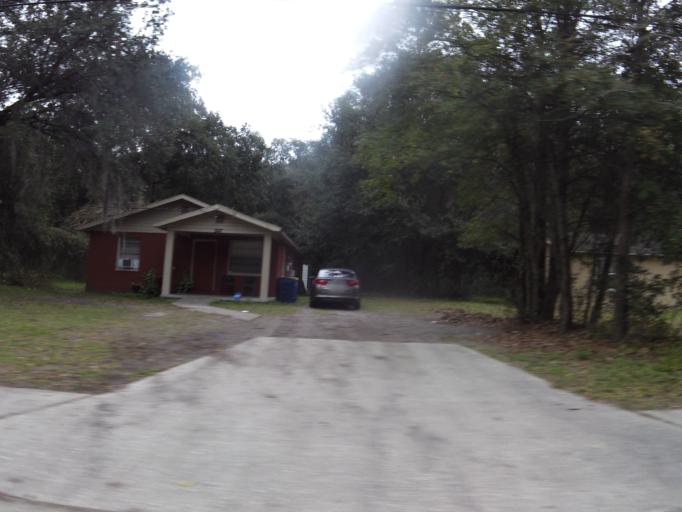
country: US
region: Florida
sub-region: Duval County
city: Jacksonville
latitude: 30.3777
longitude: -81.6968
